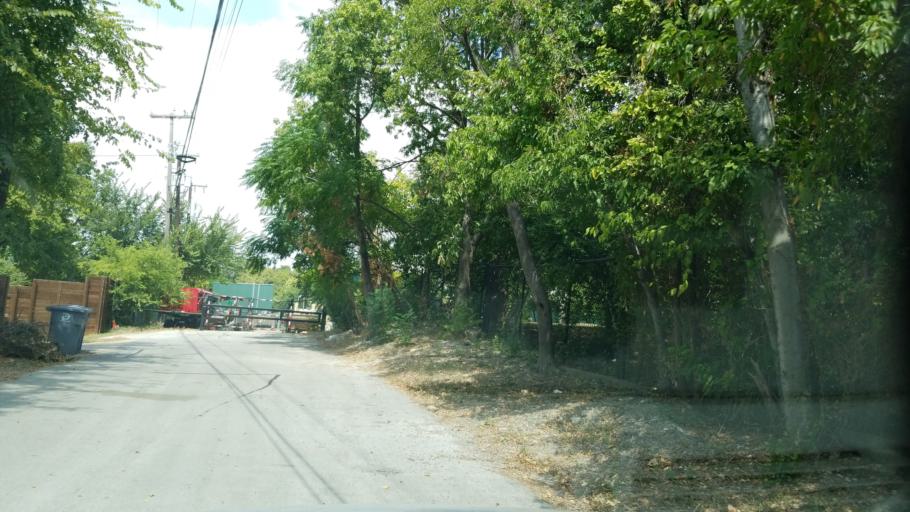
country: US
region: Texas
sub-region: Dallas County
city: Cockrell Hill
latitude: 32.7549
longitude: -96.8481
